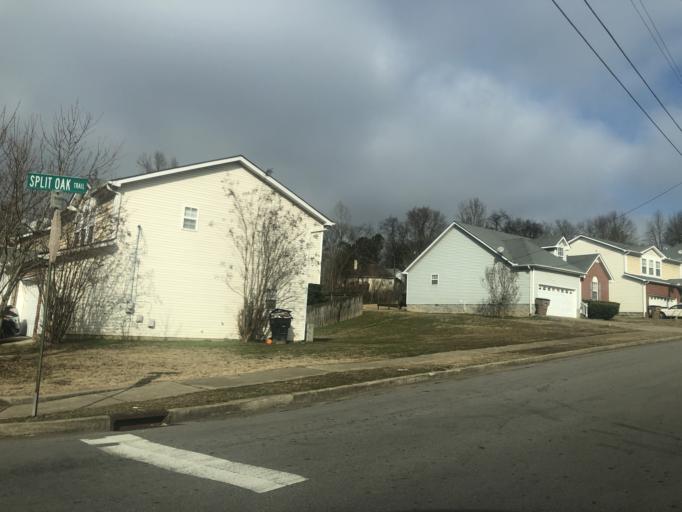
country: US
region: Tennessee
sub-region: Rutherford County
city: La Vergne
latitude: 36.0756
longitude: -86.6550
